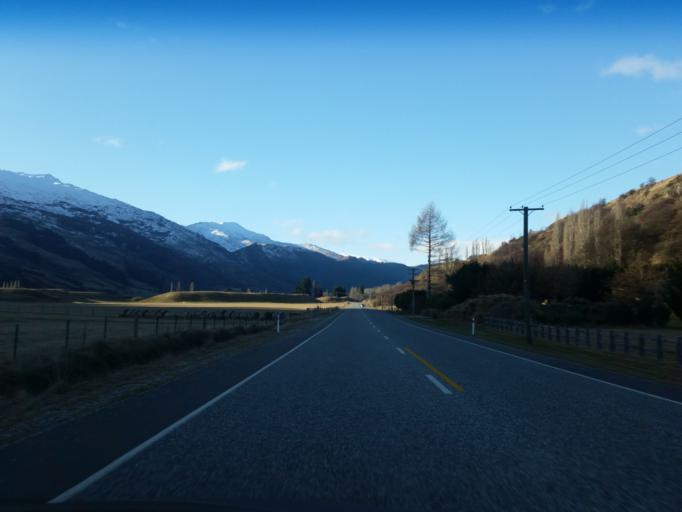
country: NZ
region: Otago
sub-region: Queenstown-Lakes District
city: Queenstown
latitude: -44.9663
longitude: 168.7103
